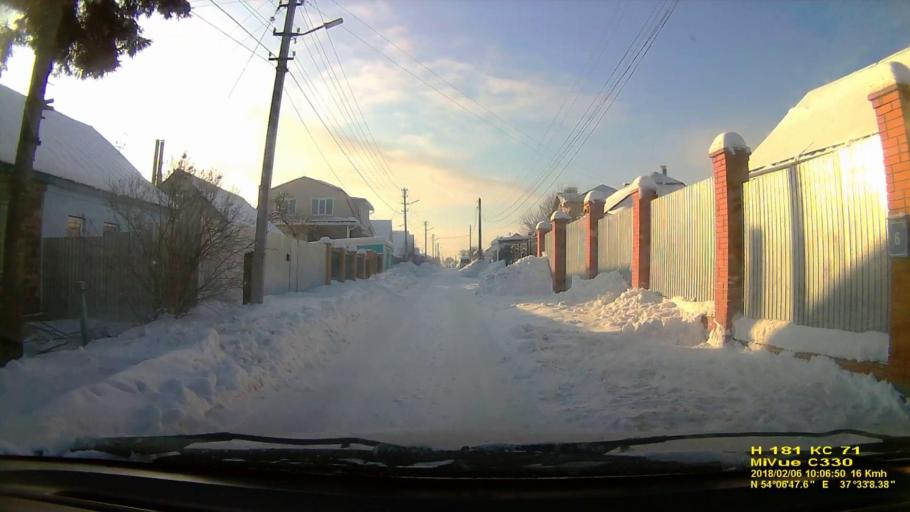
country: RU
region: Tula
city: Kosaya Gora
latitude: 54.1132
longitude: 37.5523
